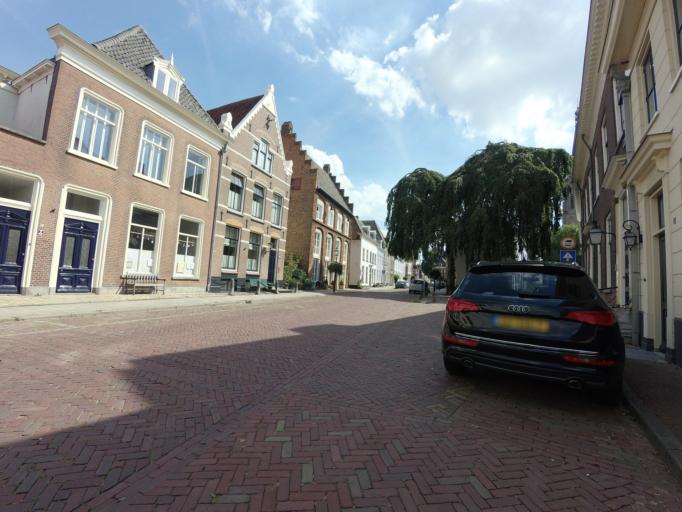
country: NL
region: Gelderland
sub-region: Gemeente Doesburg
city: Doesburg
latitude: 52.0160
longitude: 6.1333
